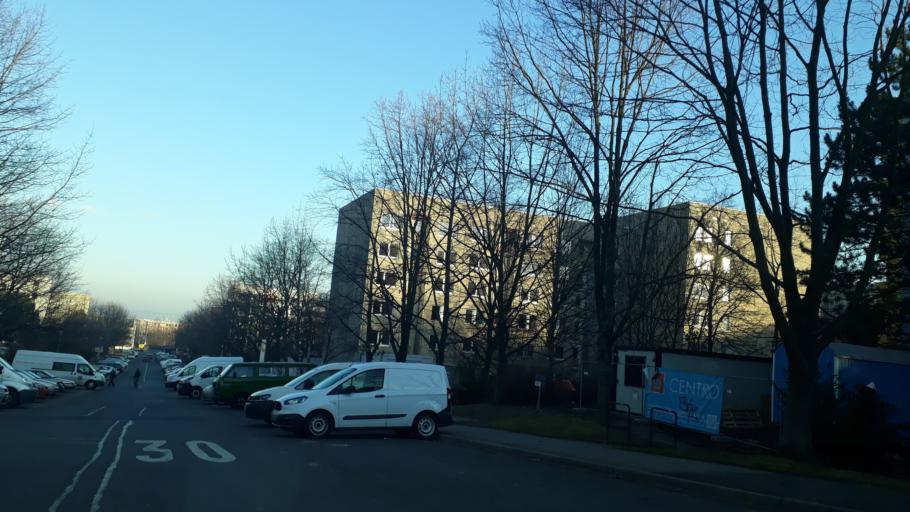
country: DE
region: Saxony
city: Freital
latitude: 51.0457
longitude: 13.6725
